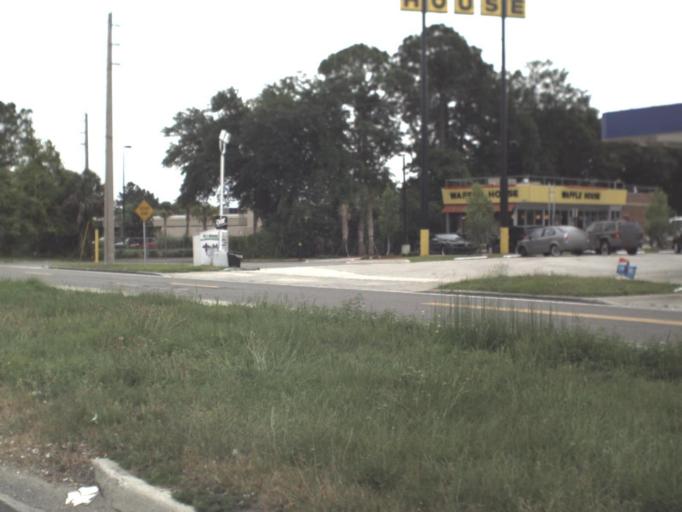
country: US
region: Florida
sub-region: Duval County
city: Jacksonville
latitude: 30.4820
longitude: -81.6470
